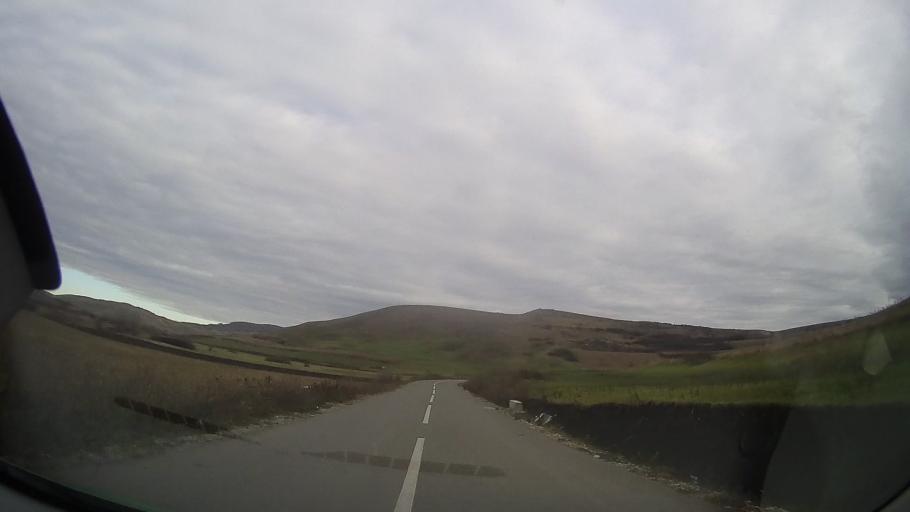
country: RO
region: Bistrita-Nasaud
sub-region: Comuna Silvasu de Campie
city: Silvasu de Campie
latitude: 46.7936
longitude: 24.2927
